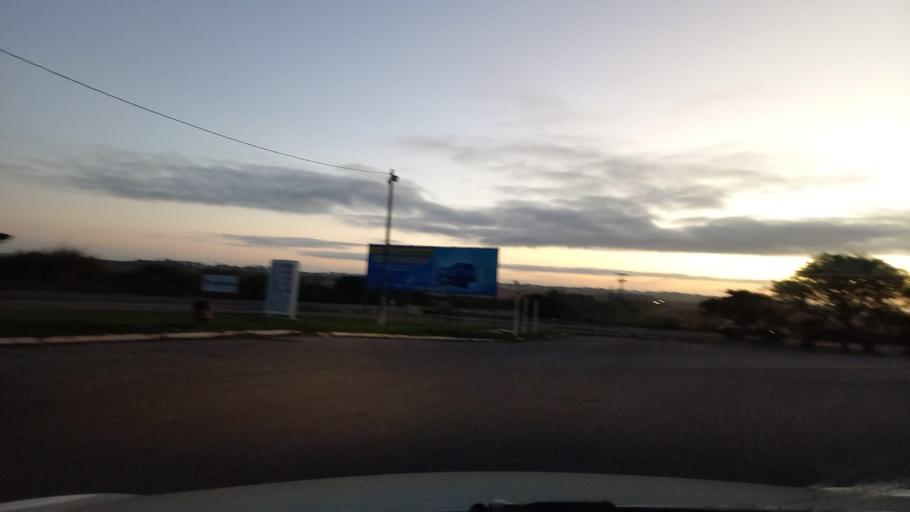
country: BR
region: Rio Grande do Sul
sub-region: Rosario Do Sul
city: Rosario do Sul
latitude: -30.2395
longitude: -54.8704
